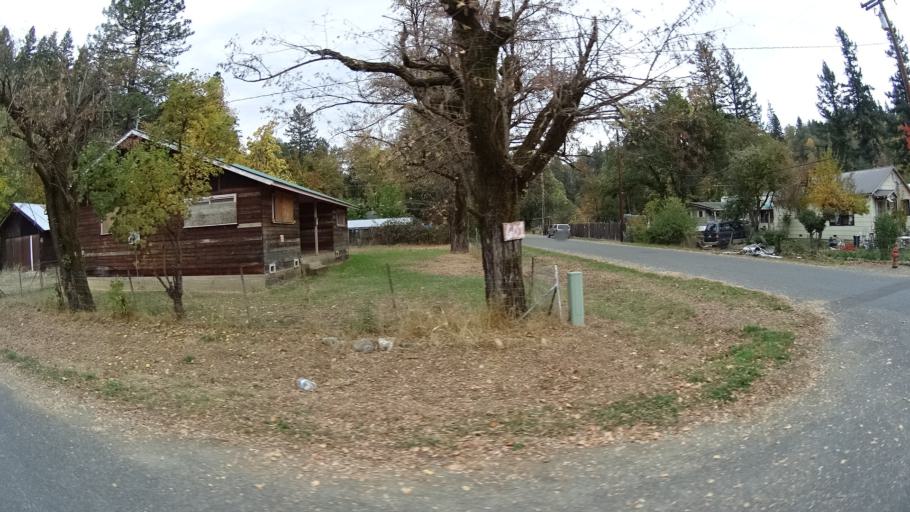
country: US
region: California
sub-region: Siskiyou County
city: Happy Camp
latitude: 41.8000
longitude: -123.3804
